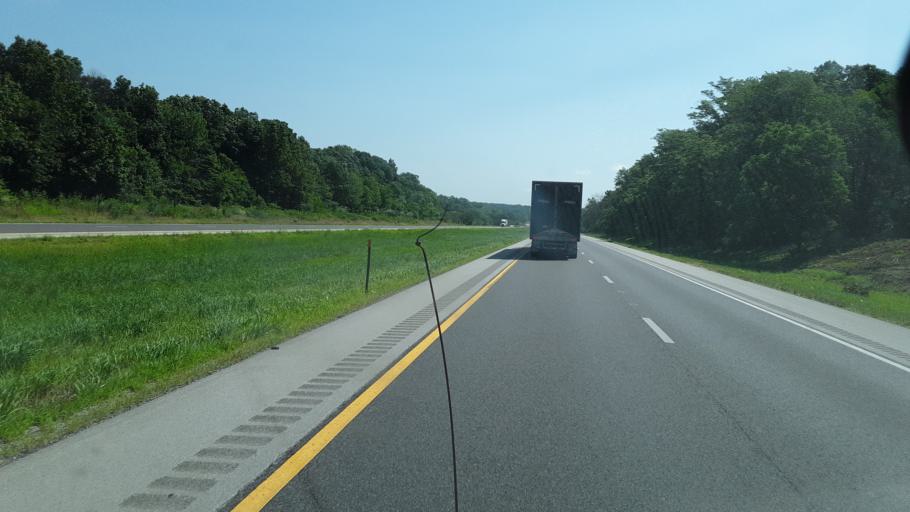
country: US
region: Illinois
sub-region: Cumberland County
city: Toledo
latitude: 39.2000
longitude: -88.3002
